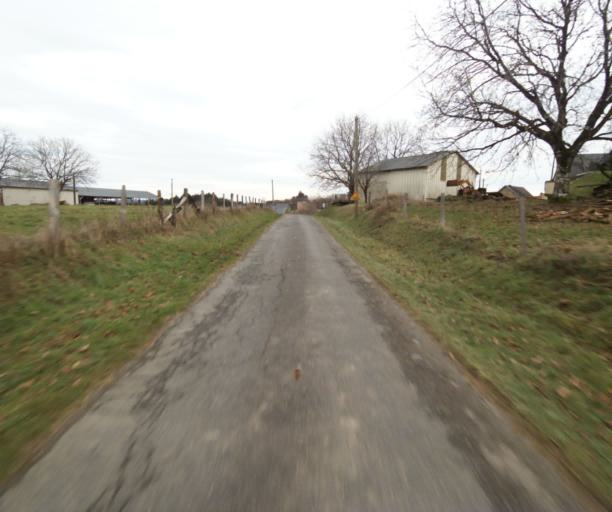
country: FR
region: Limousin
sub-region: Departement de la Correze
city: Cornil
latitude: 45.2277
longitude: 1.6739
